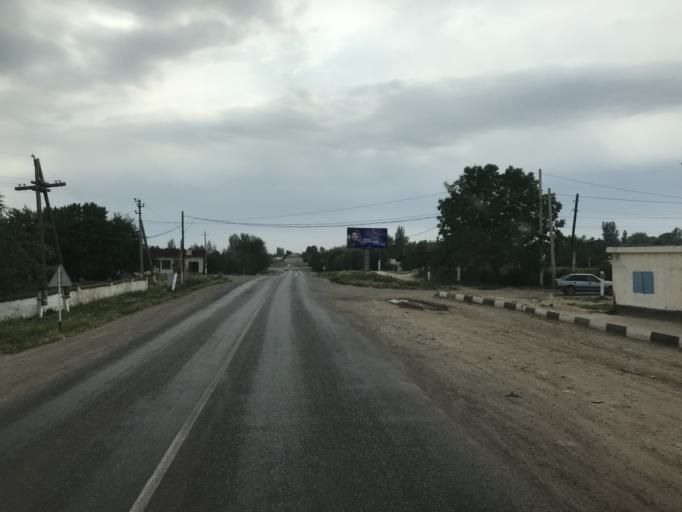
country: KZ
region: Ongtustik Qazaqstan
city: Saryaghash
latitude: 41.3734
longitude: 69.0013
